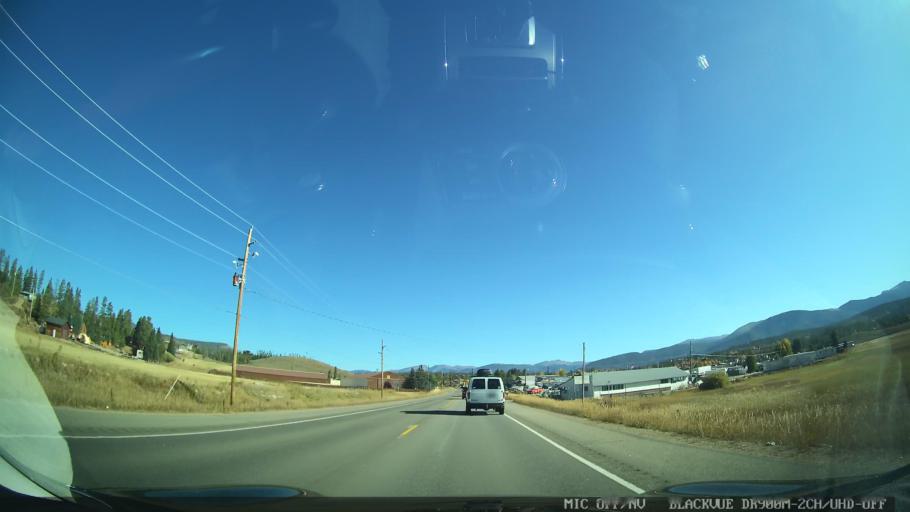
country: US
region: Colorado
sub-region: Grand County
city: Granby
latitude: 40.1892
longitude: -105.8819
